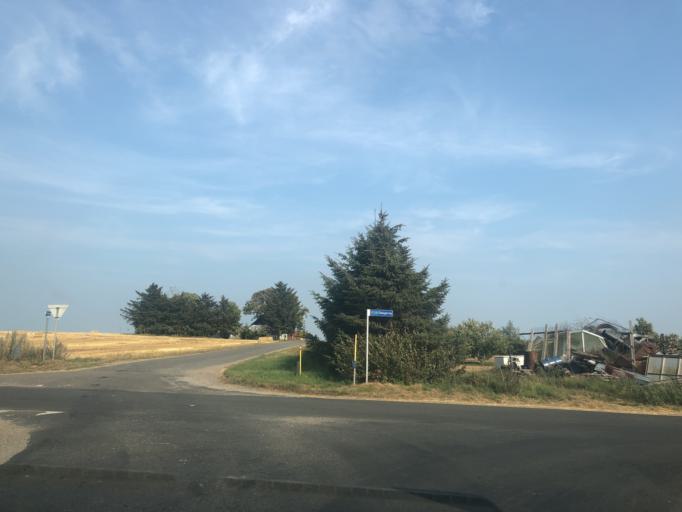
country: DK
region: North Denmark
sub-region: Morso Kommune
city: Nykobing Mors
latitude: 56.8222
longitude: 9.0211
